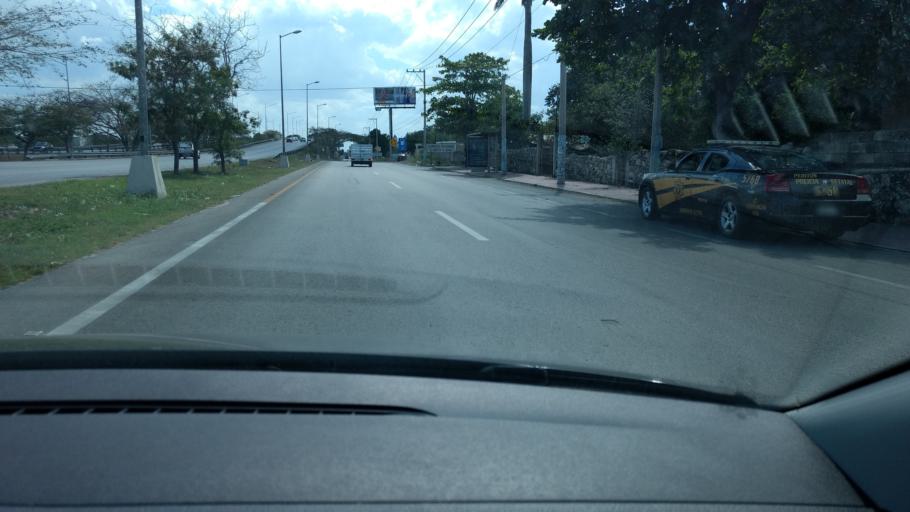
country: MX
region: Yucatan
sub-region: Kanasin
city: Kanasin
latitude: 20.9715
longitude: -89.5656
